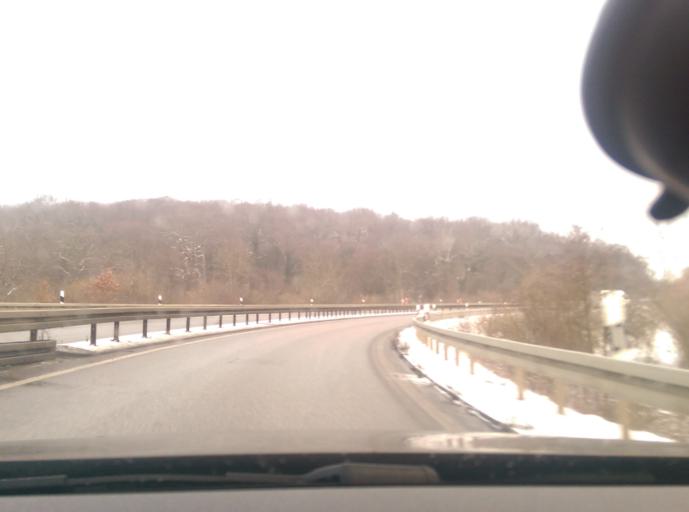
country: DE
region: Hesse
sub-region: Regierungsbezirk Kassel
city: Lohfelden
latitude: 51.2962
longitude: 9.5602
